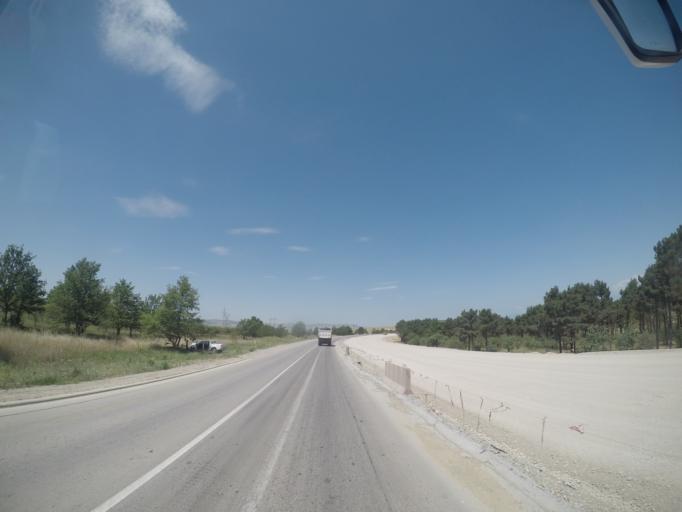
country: AZ
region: Qobustan
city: Qobustan
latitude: 40.5279
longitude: 48.7936
